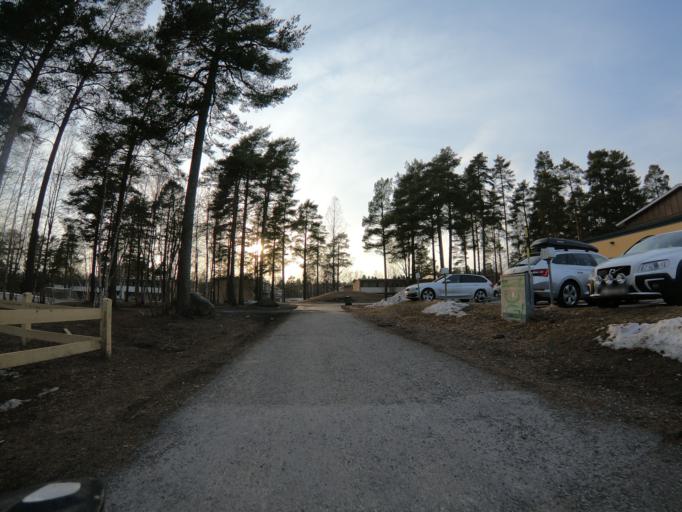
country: SE
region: Vaesterbotten
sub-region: Umea Kommun
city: Umea
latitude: 63.8415
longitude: 20.2810
